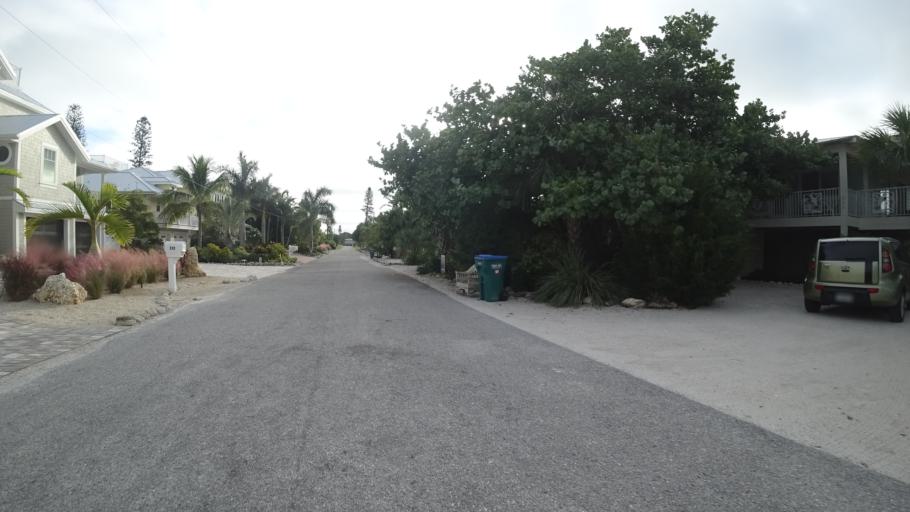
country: US
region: Florida
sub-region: Manatee County
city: Holmes Beach
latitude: 27.5039
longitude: -82.7157
